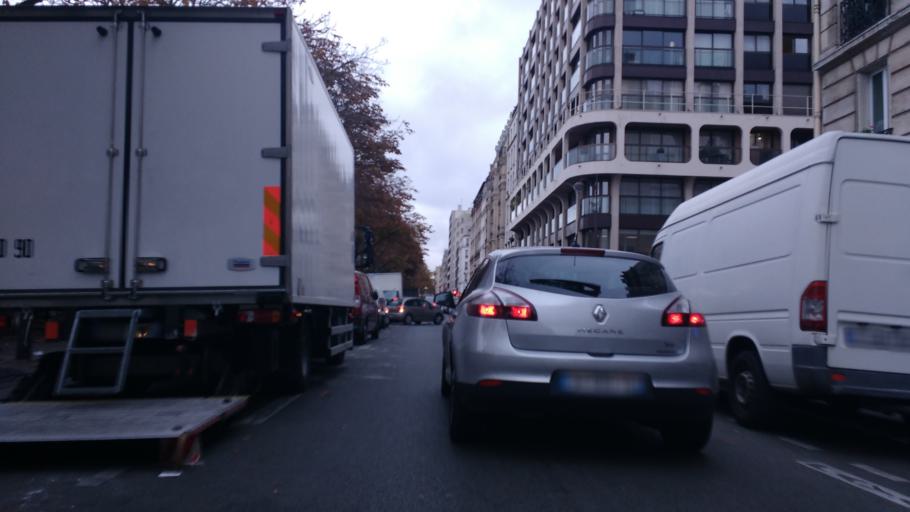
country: FR
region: Ile-de-France
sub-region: Departement du Val-de-Marne
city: Saint-Mande
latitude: 48.8474
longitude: 2.4041
